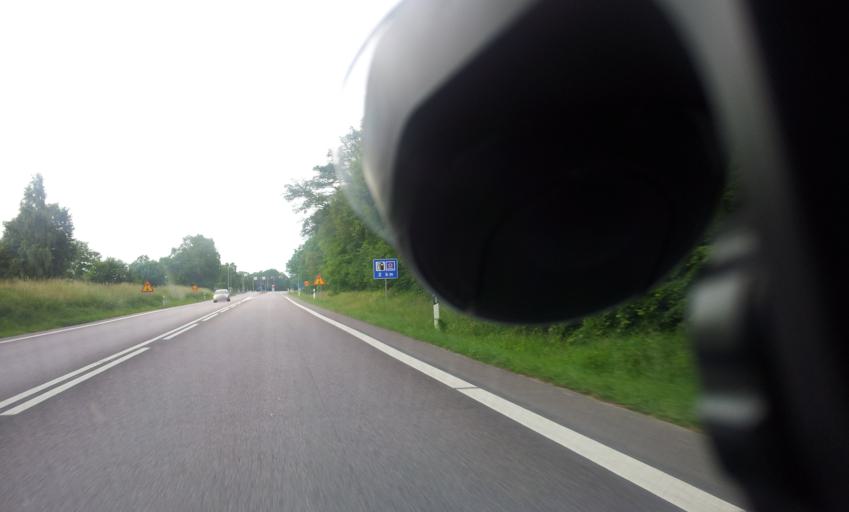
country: SE
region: Kalmar
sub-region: Monsteras Kommun
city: Moensteras
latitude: 57.0548
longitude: 16.4399
